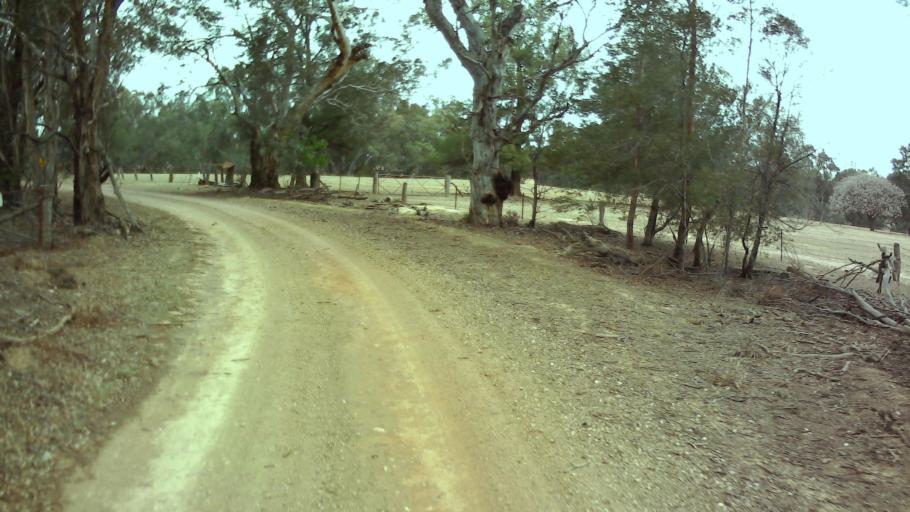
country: AU
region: New South Wales
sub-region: Weddin
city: Grenfell
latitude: -33.9296
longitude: 148.2608
